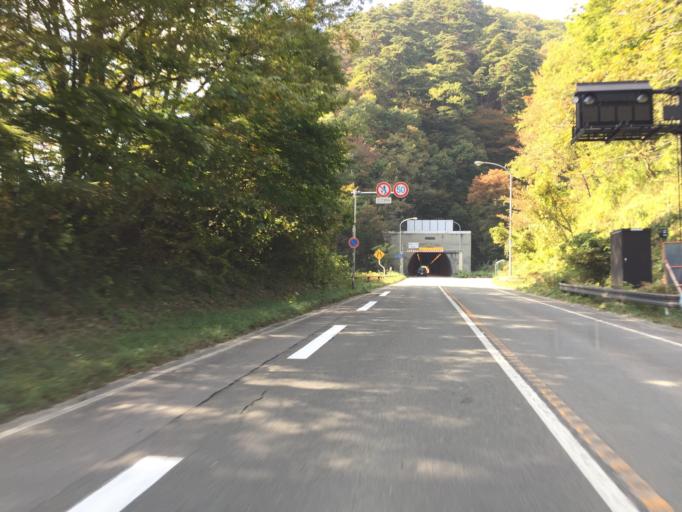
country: JP
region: Fukushima
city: Fukushima-shi
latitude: 37.8368
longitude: 140.3806
